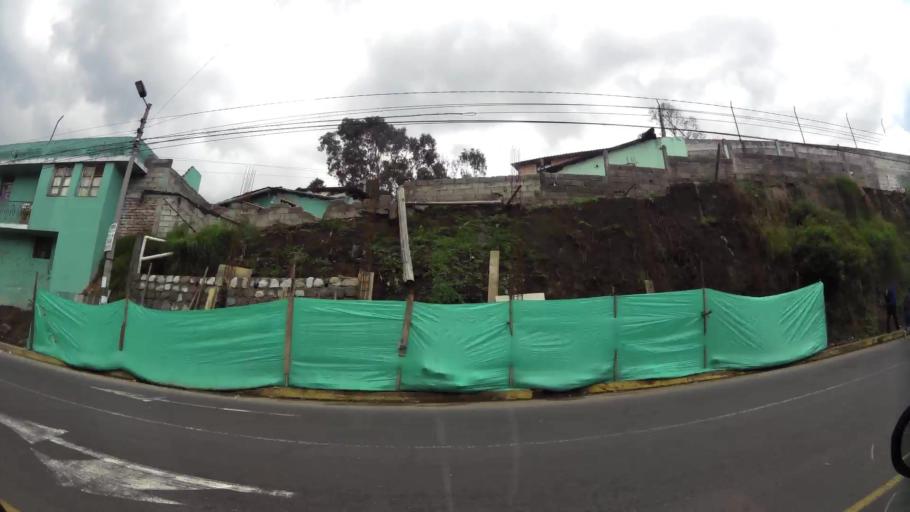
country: EC
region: Pichincha
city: Quito
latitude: -0.2412
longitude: -78.4988
